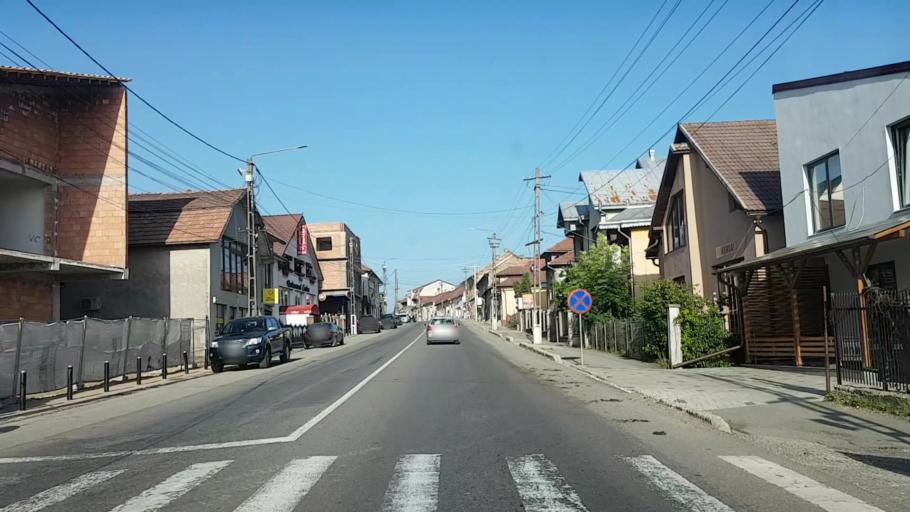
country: RO
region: Bistrita-Nasaud
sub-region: Comuna Prundu Bargaului
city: Susenii Bargaului
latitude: 47.2197
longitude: 24.7365
